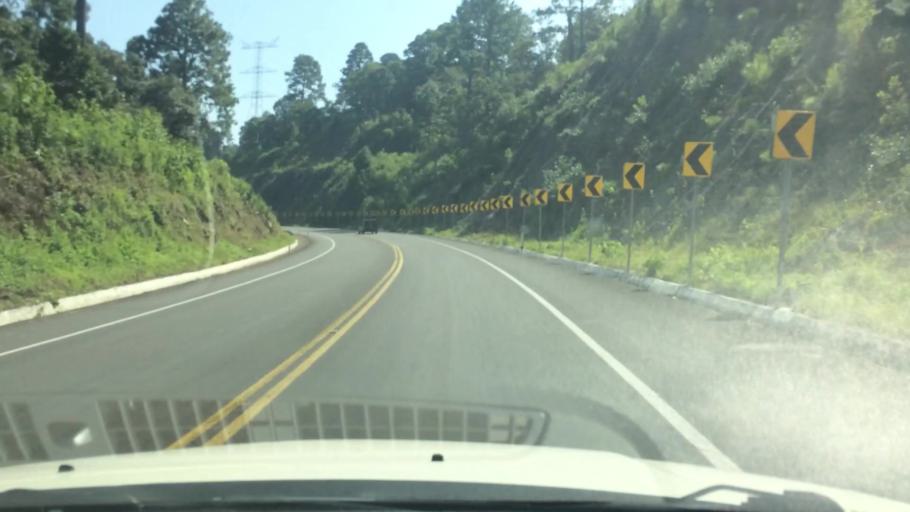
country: MX
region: Mexico
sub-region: Amanalco
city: Polvillos (San Bartolo Quinta Seccion)
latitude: 19.2197
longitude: -100.0897
